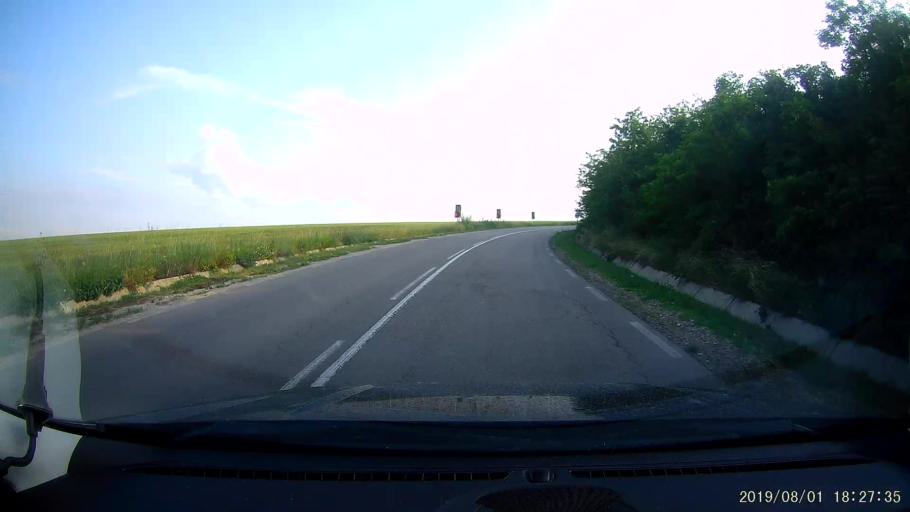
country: BG
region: Shumen
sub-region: Obshtina Venets
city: Venets
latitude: 43.5841
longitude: 26.9807
